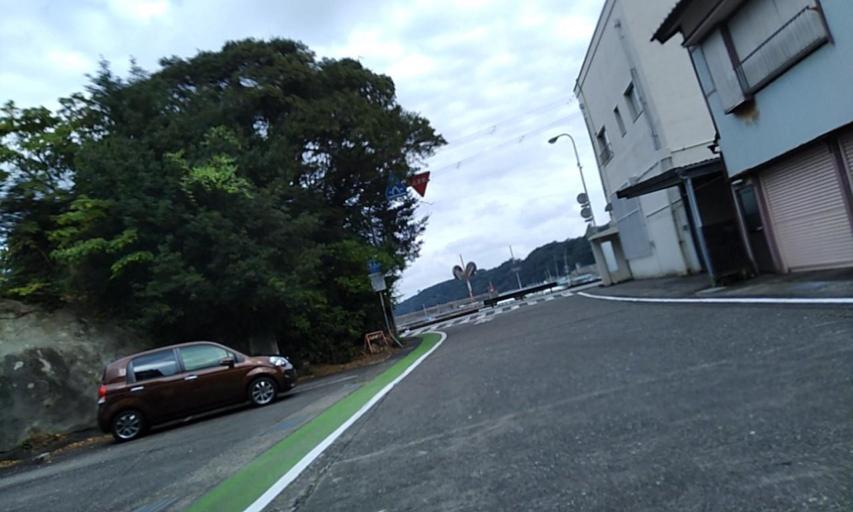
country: JP
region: Wakayama
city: Shingu
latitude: 33.5909
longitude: 135.9448
